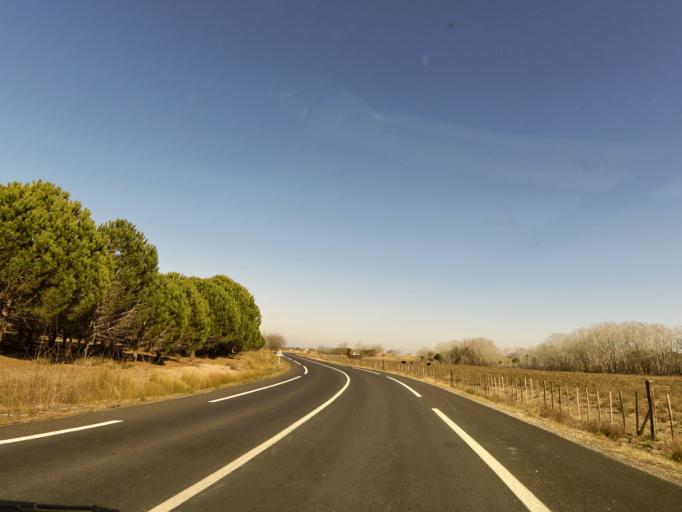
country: FR
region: Languedoc-Roussillon
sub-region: Departement du Gard
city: Aigues-Mortes
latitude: 43.5859
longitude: 4.2106
